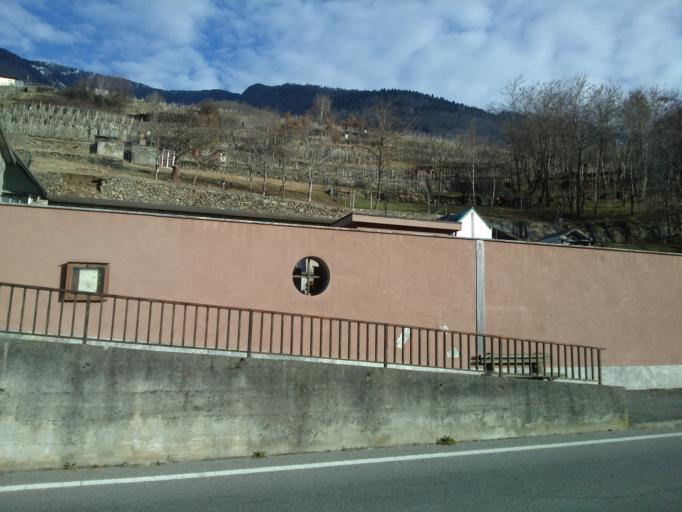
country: IT
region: Lombardy
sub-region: Provincia di Sondrio
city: Villapinta
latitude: 46.1752
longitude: 9.6834
